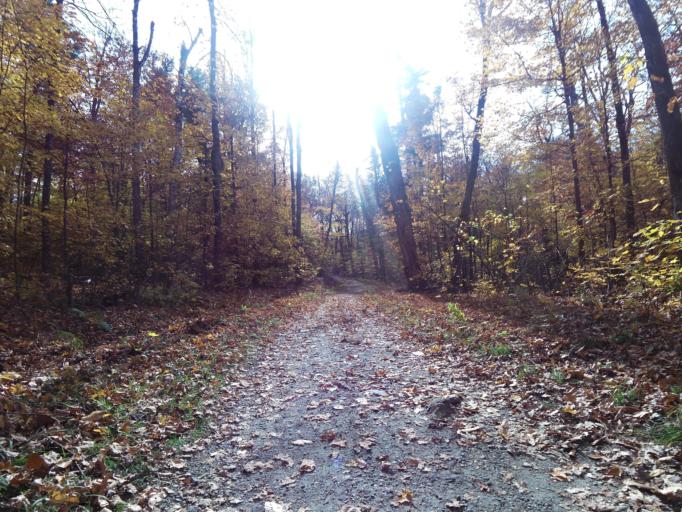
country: CA
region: Quebec
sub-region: Outaouais
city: Wakefield
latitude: 45.5041
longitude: -75.8750
